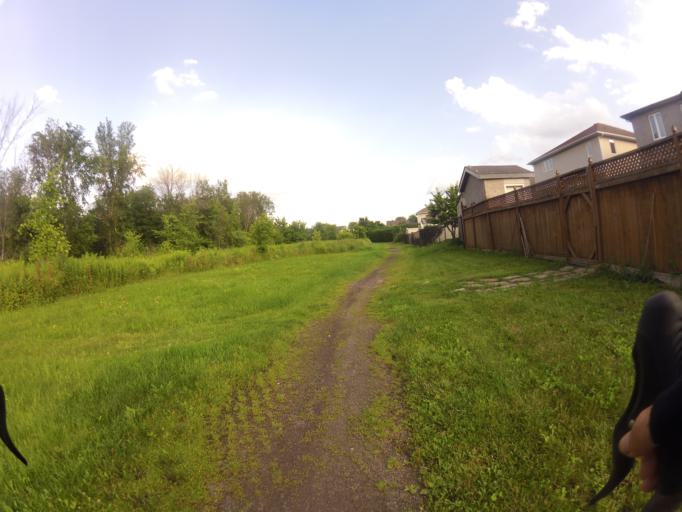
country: CA
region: Ontario
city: Ottawa
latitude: 45.2883
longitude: -75.6838
